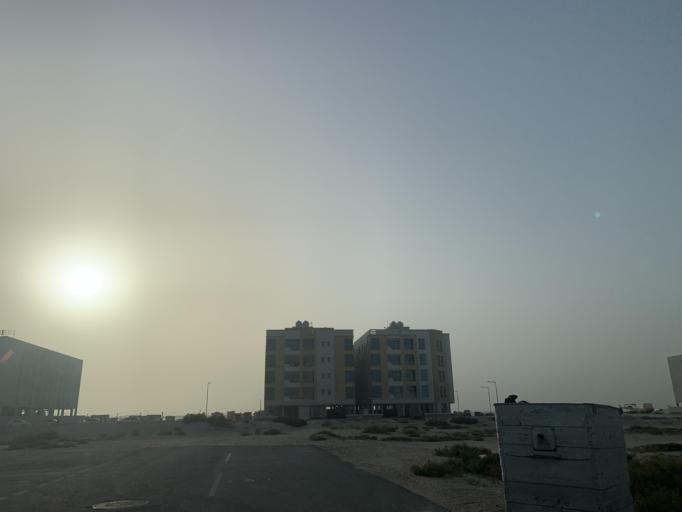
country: BH
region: Manama
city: Jidd Hafs
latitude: 26.2383
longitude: 50.5267
